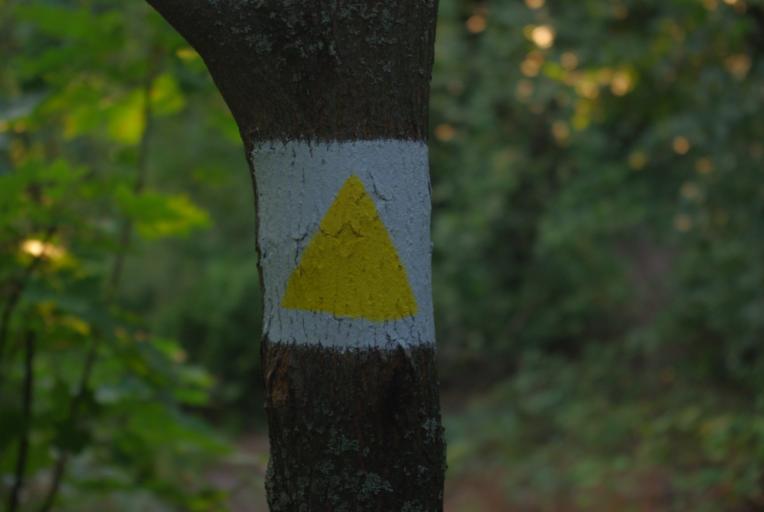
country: HU
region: Pest
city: Solymar
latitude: 47.5764
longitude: 18.9624
